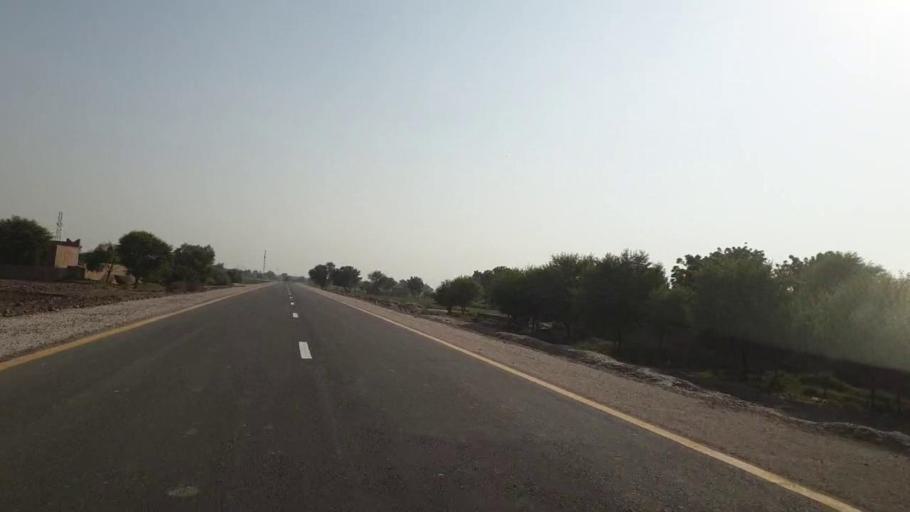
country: PK
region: Sindh
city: Bhan
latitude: 26.4871
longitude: 67.7796
